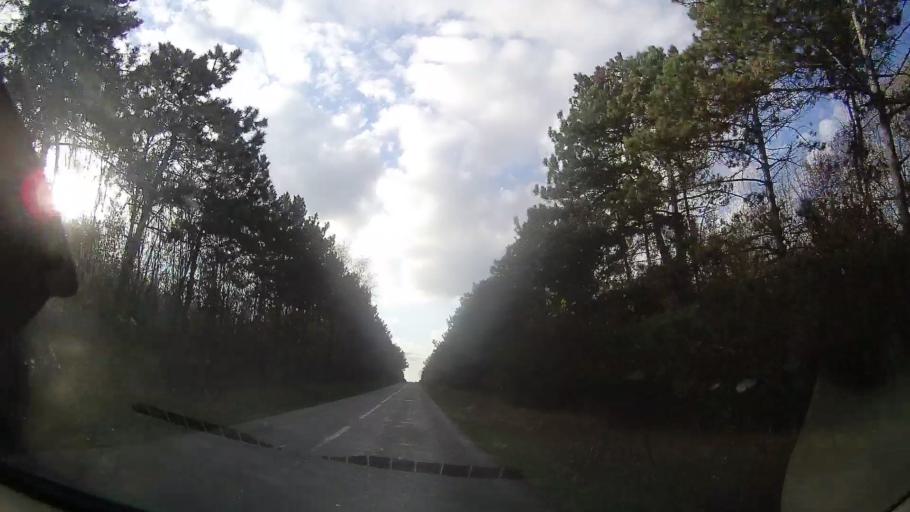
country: RO
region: Constanta
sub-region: Comuna Negru Voda
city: Negru Voda
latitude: 43.8193
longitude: 28.2764
